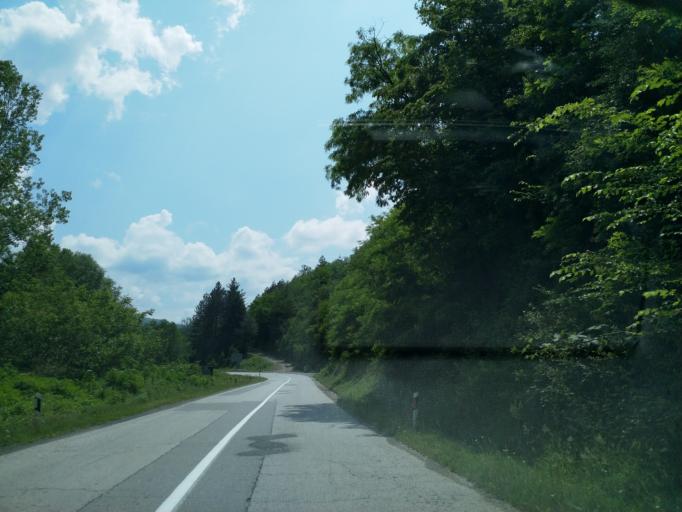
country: RS
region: Central Serbia
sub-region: Rasinski Okrug
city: Aleksandrovac
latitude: 43.3706
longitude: 20.9967
